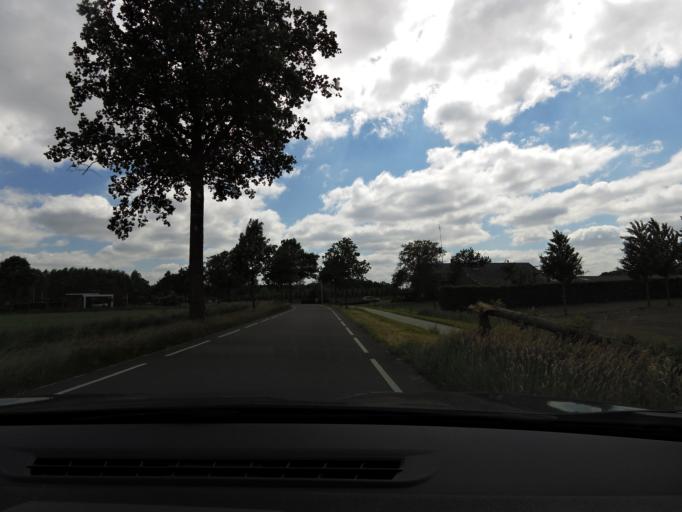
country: NL
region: North Brabant
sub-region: Gemeente Loon op Zand
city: Loon op Zand
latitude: 51.6234
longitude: 5.1231
